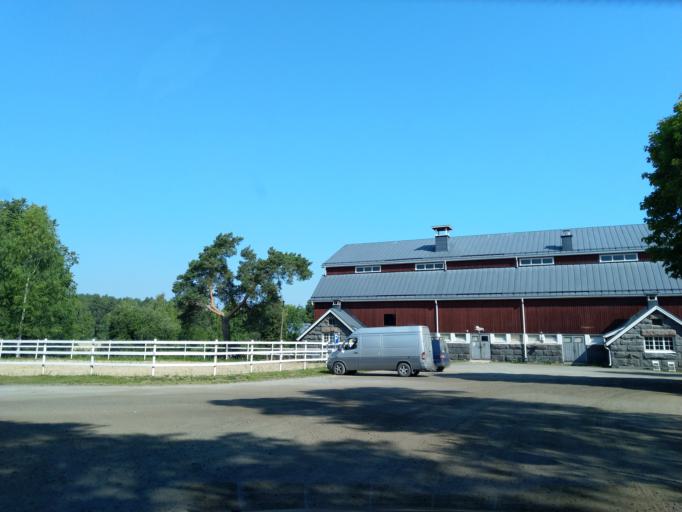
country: FI
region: Satakunta
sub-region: Pori
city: Noormarkku
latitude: 61.5946
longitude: 21.8834
